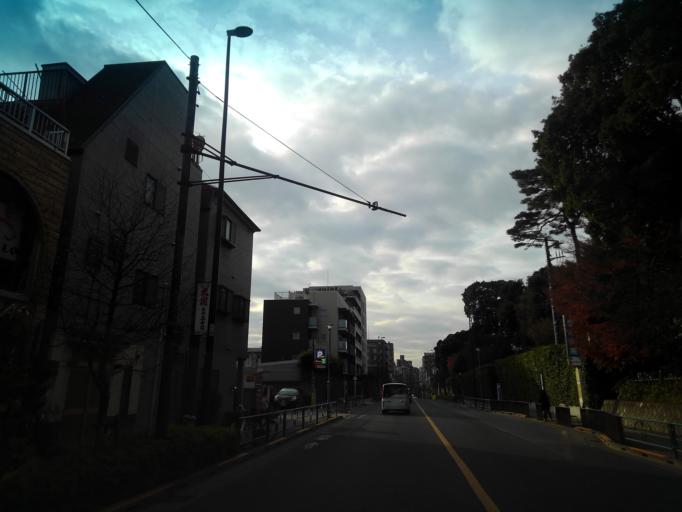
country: JP
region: Tokyo
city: Tanashicho
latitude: 35.7104
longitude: 139.5079
